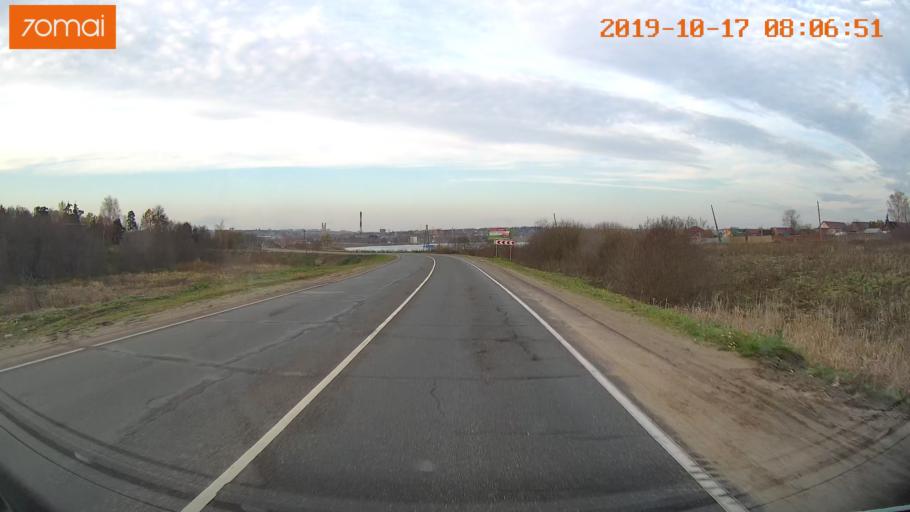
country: RU
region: Vladimir
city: Kol'chugino
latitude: 56.3198
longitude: 39.4071
